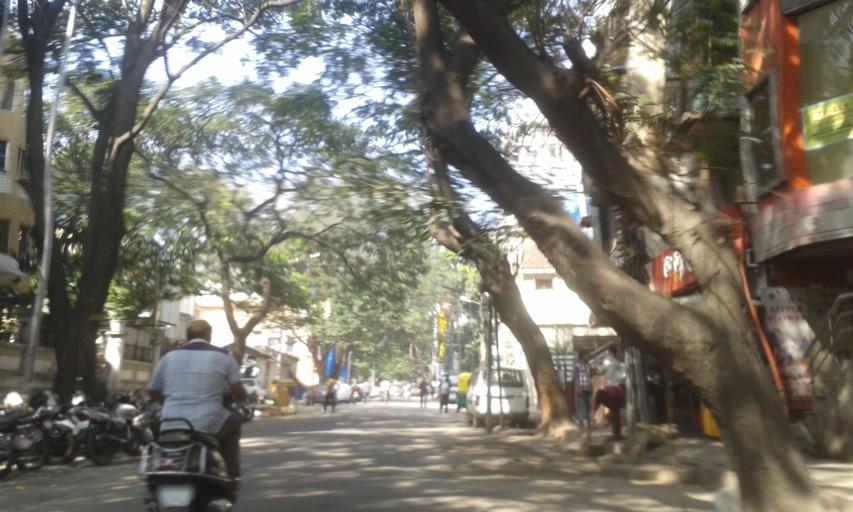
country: IN
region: Karnataka
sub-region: Bangalore Urban
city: Bangalore
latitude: 12.9672
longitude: 77.6086
